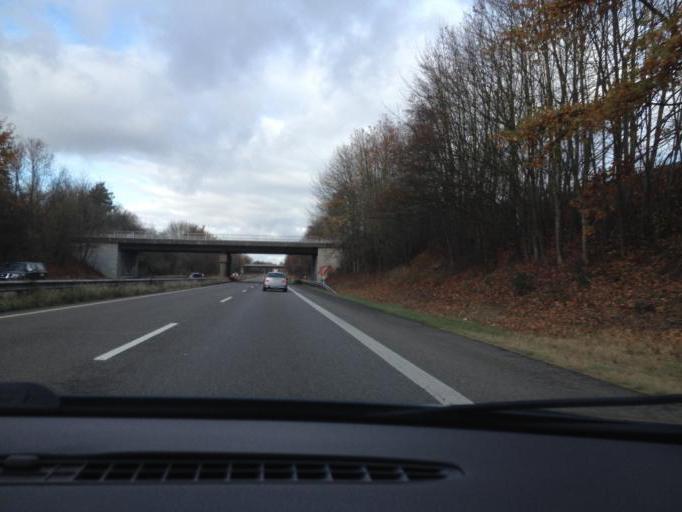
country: DE
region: Rheinland-Pfalz
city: Westheim
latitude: 49.2452
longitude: 8.3325
